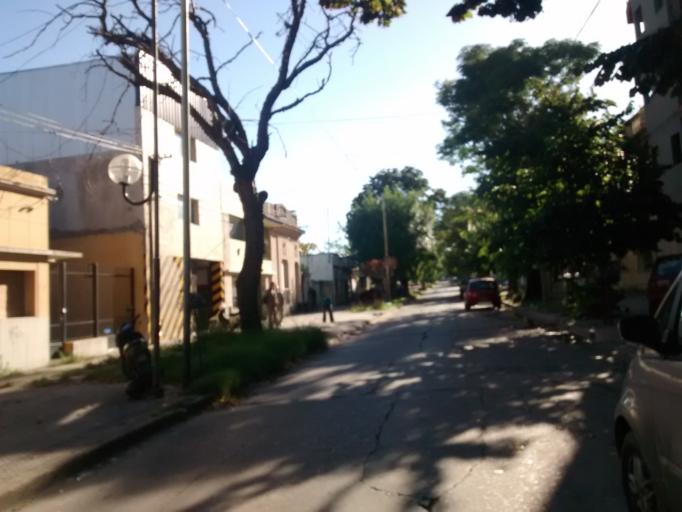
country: AR
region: Buenos Aires
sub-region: Partido de La Plata
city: La Plata
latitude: -34.9343
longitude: -57.9502
